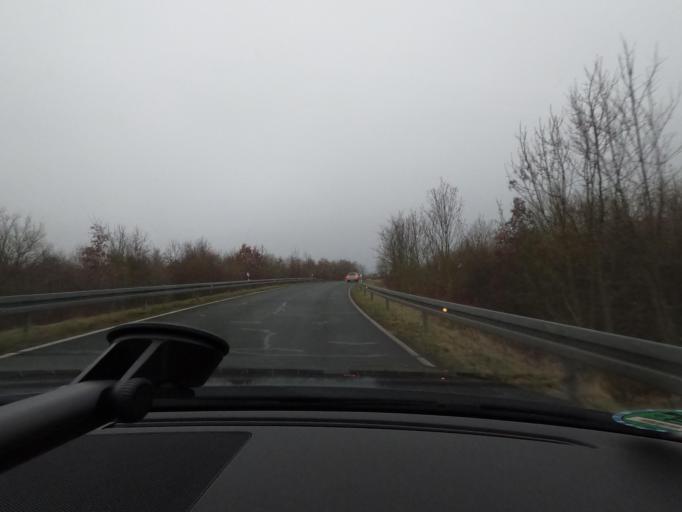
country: DE
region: Thuringia
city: Behringen
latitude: 50.7940
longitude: 11.0065
